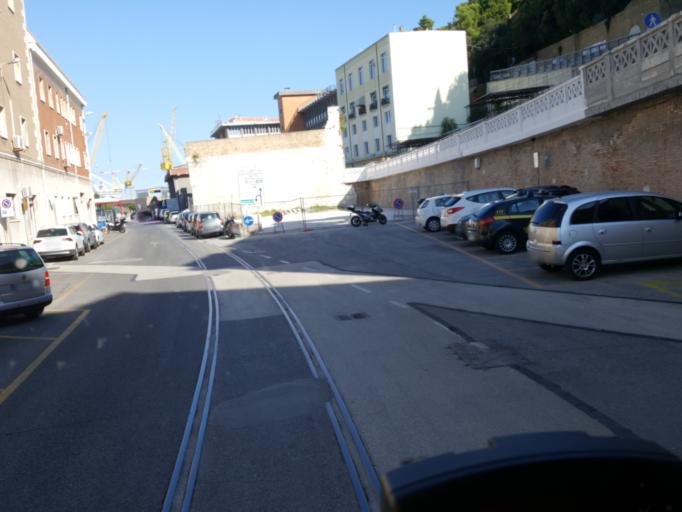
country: IT
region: The Marches
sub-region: Provincia di Ancona
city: Le Grazie di Ancona
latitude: 43.6230
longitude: 13.5100
